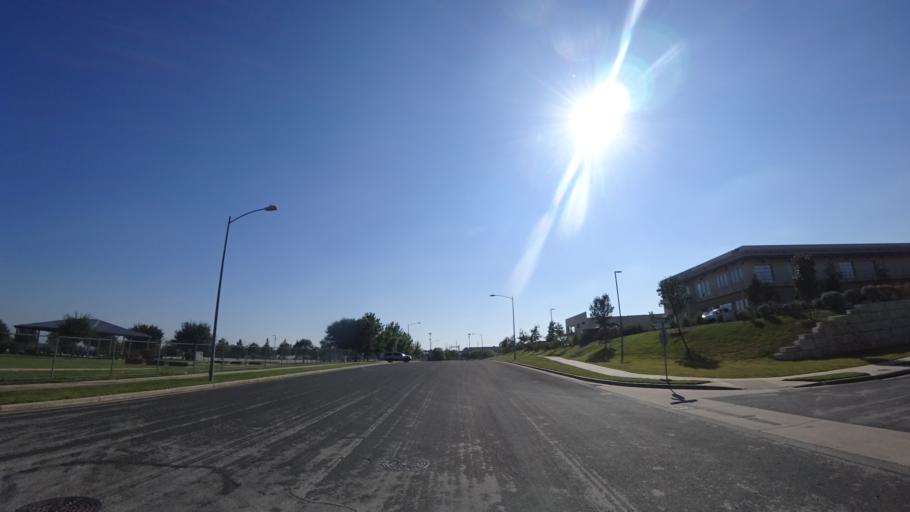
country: US
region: Texas
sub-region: Travis County
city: Austin
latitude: 30.3440
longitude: -97.6837
